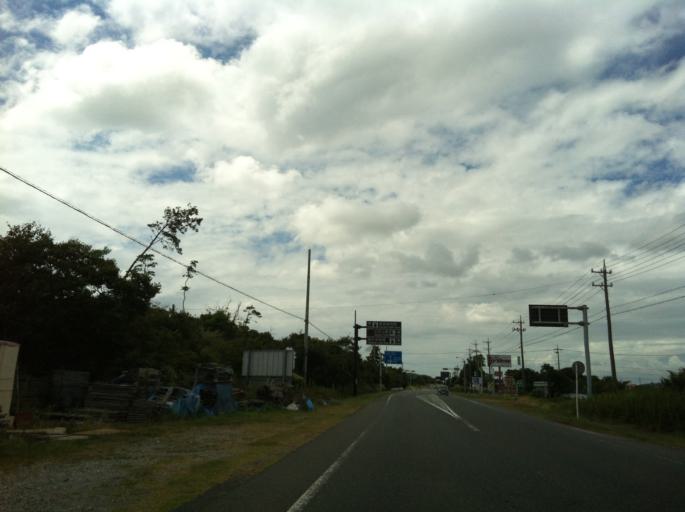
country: JP
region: Shizuoka
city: Kakegawa
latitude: 34.6580
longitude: 138.0462
